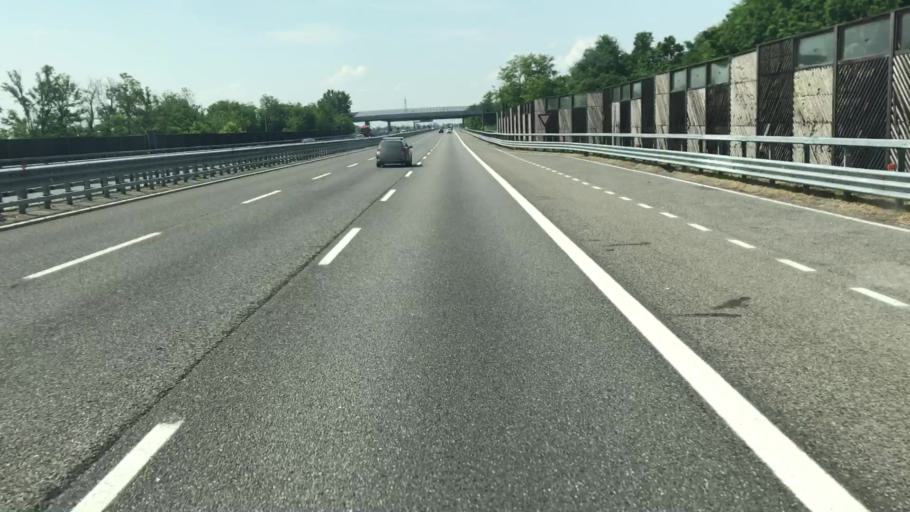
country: IT
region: Lombardy
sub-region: Citta metropolitana di Milano
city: Binasco
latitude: 45.3302
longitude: 9.0919
